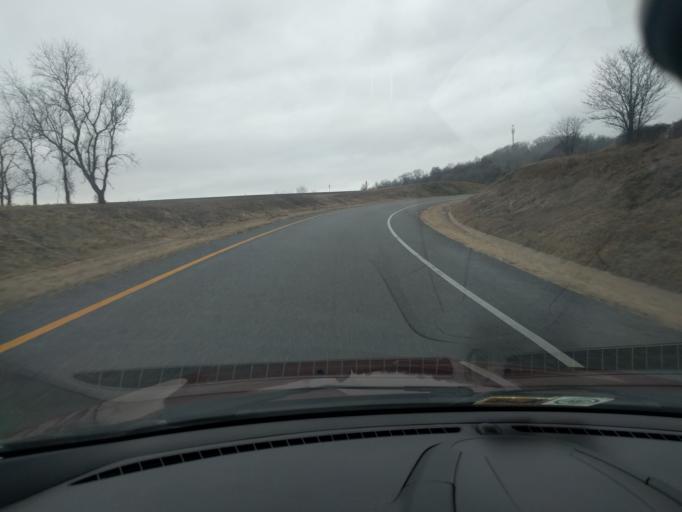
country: US
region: Virginia
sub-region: Augusta County
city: Jolivue
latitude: 38.1097
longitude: -79.0607
